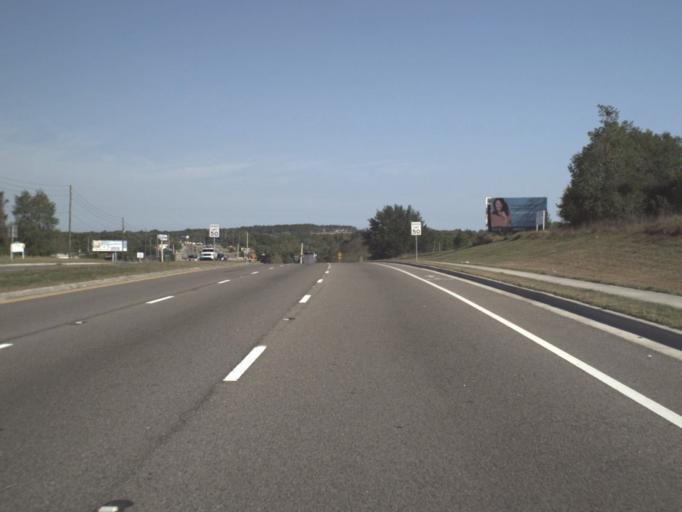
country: US
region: Florida
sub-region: Lake County
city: Minneola
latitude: 28.5692
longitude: -81.7448
